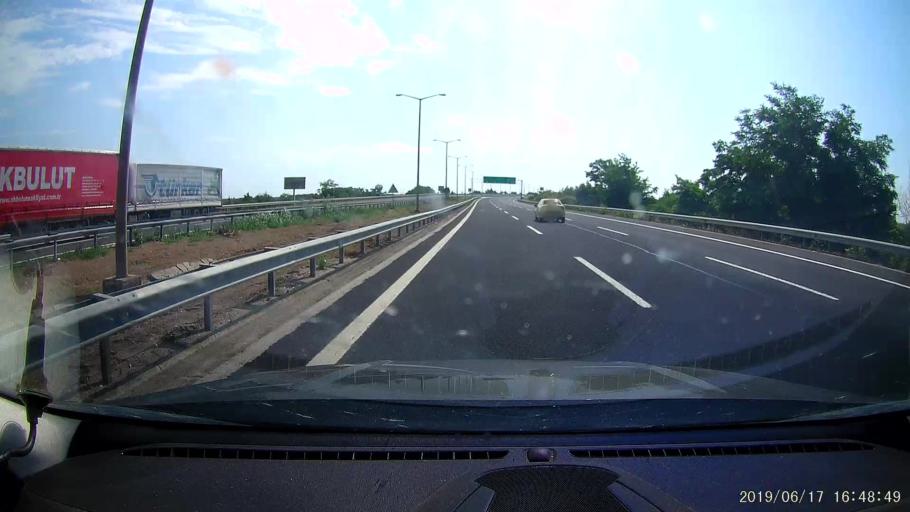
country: TR
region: Kirklareli
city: Babaeski
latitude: 41.5061
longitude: 27.1311
